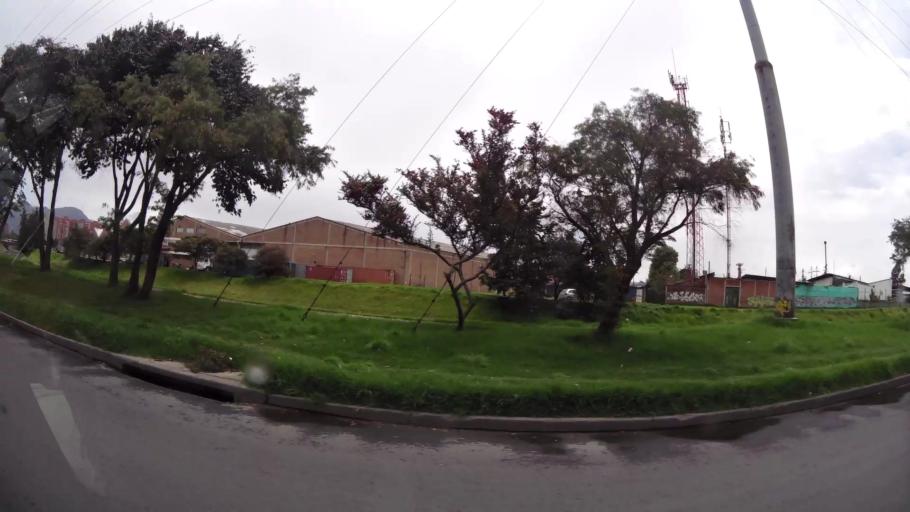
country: CO
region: Bogota D.C.
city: Bogota
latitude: 4.6493
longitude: -74.1116
